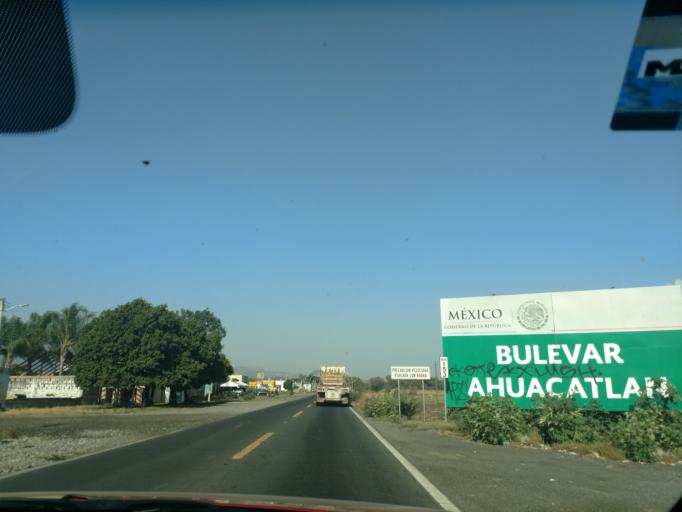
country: MX
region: Nayarit
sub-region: Ahuacatlan
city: Ahuacatlan
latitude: 21.0592
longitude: -104.4978
